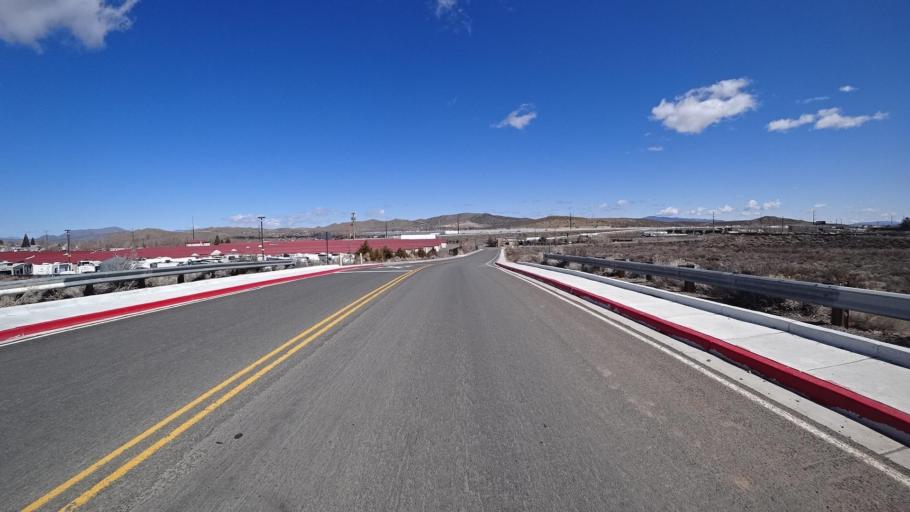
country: US
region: Nevada
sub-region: Washoe County
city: Golden Valley
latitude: 39.5961
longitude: -119.8417
